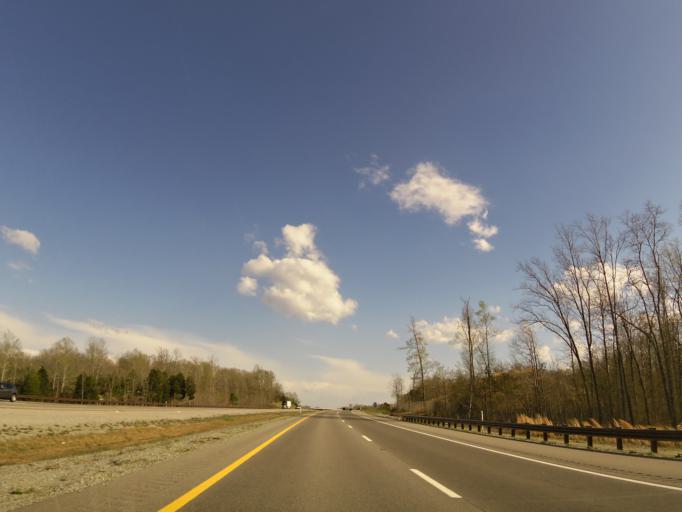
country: US
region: Tennessee
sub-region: Williamson County
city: Fairview
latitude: 35.8705
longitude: -87.0916
